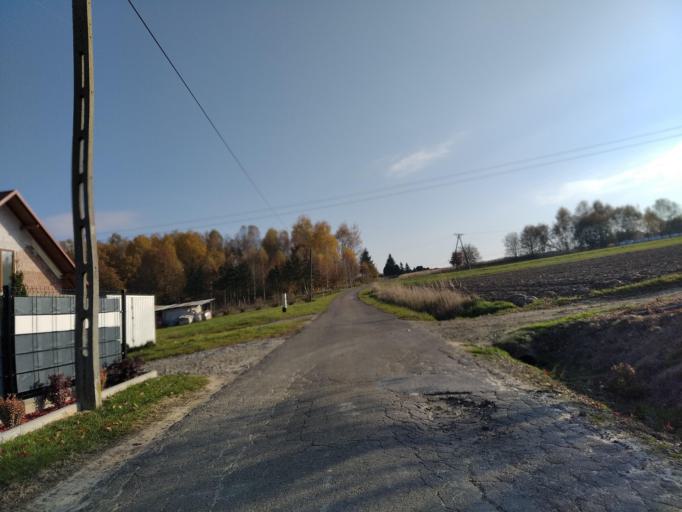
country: PL
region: Subcarpathian Voivodeship
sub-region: Powiat strzyzowski
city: Czudec
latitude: 49.9020
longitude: 21.8417
